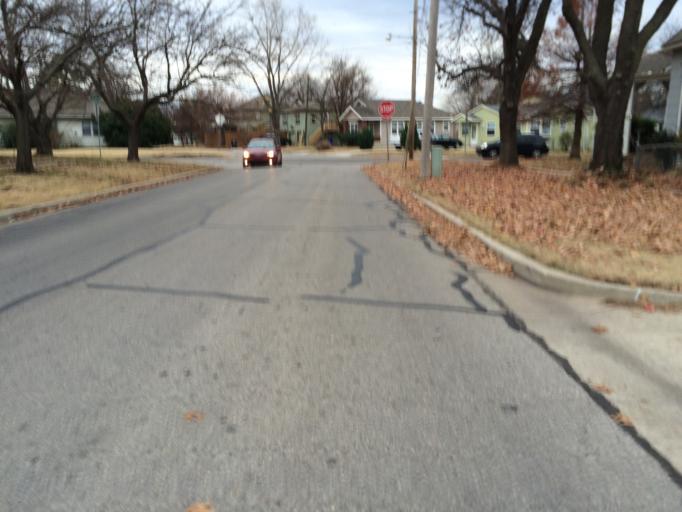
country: US
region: Oklahoma
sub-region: Cleveland County
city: Norman
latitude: 35.2261
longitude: -97.4427
